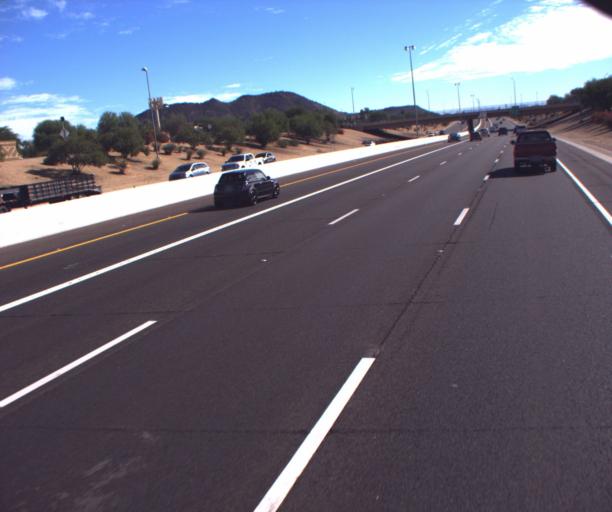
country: US
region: Arizona
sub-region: Maricopa County
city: Peoria
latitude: 33.6681
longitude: -112.1893
